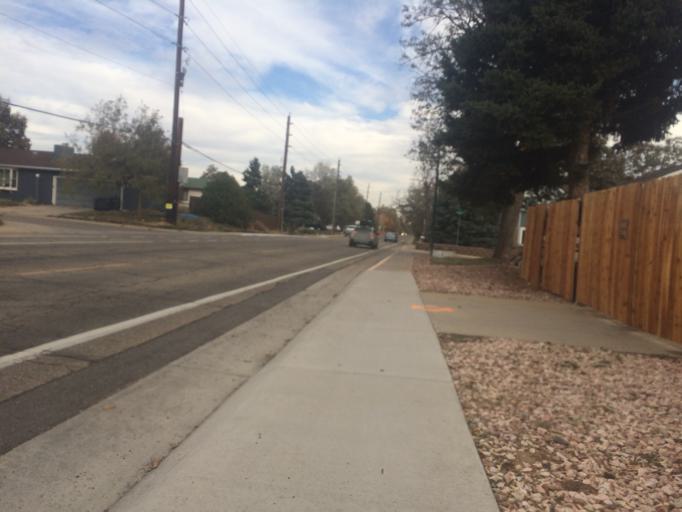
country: US
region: Colorado
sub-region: Boulder County
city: Lafayette
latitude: 39.9942
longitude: -105.0979
